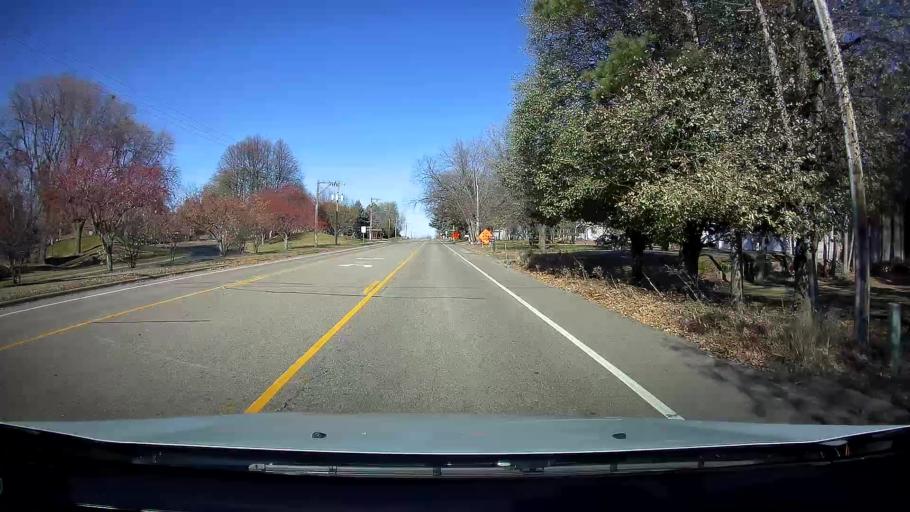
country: US
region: Minnesota
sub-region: Ramsey County
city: Shoreview
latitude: 45.0744
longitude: -93.1575
